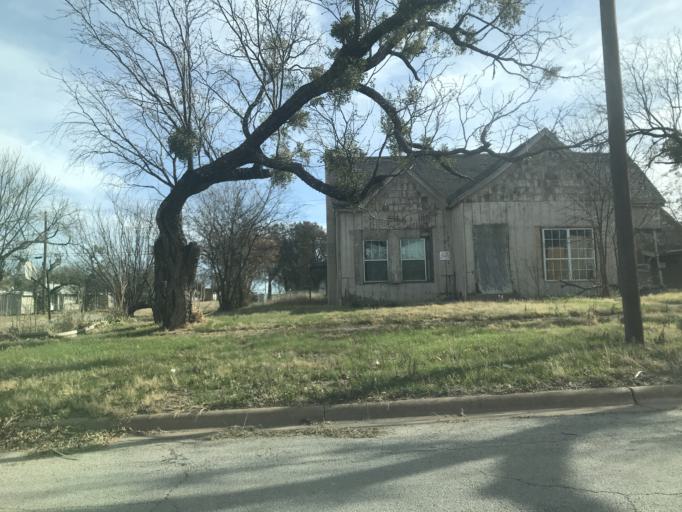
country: US
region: Texas
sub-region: Taylor County
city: Abilene
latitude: 32.4448
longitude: -99.7411
